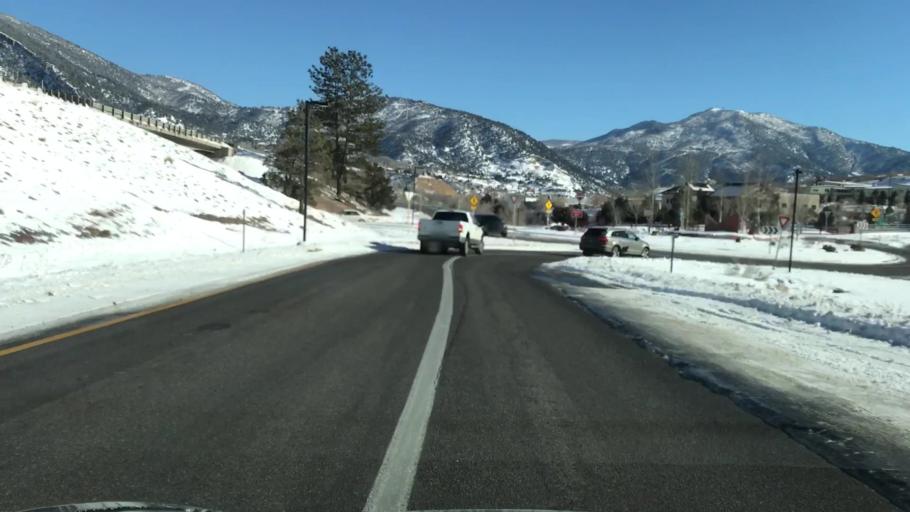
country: US
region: Colorado
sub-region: Garfield County
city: Glenwood Springs
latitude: 39.5603
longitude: -107.3622
